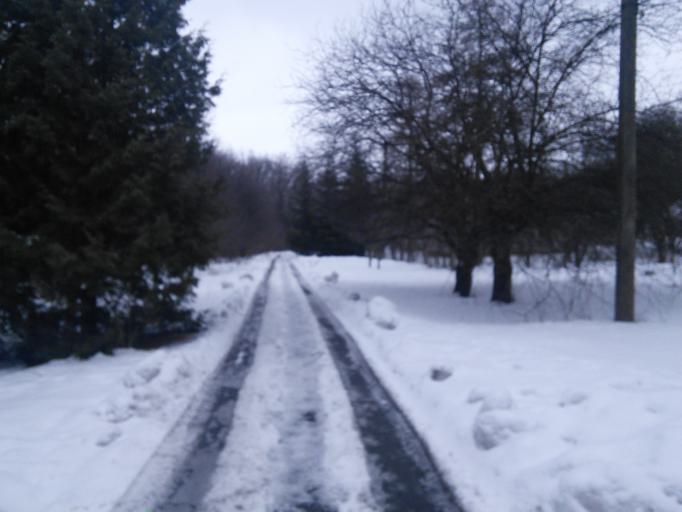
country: RU
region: Kursk
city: Chernitsyno
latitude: 51.5685
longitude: 36.0862
